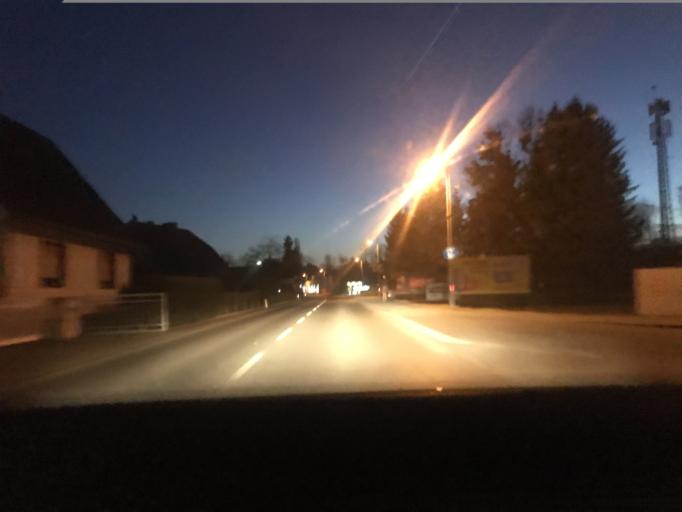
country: AT
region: Styria
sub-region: Politischer Bezirk Leibnitz
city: Kaindorf an der Sulm
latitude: 46.7920
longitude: 15.5515
